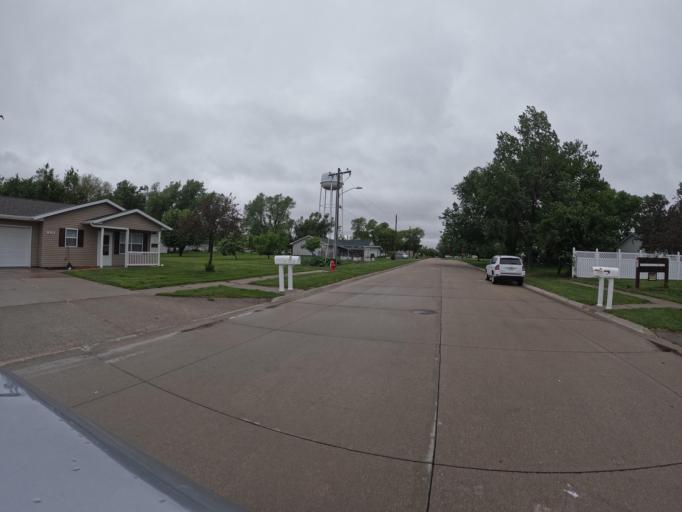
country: US
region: Nebraska
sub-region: Clay County
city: Harvard
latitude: 40.6243
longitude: -98.0935
